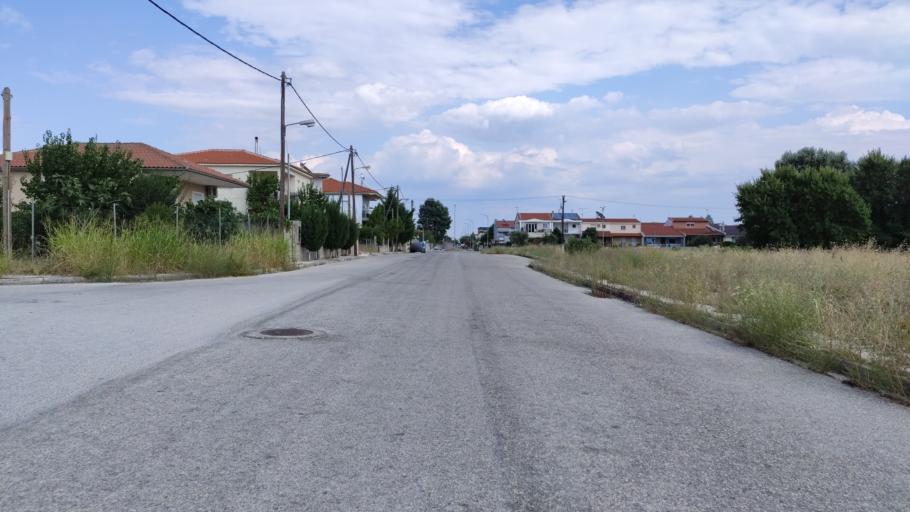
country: GR
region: East Macedonia and Thrace
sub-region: Nomos Rodopis
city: Komotini
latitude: 41.1295
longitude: 25.3942
